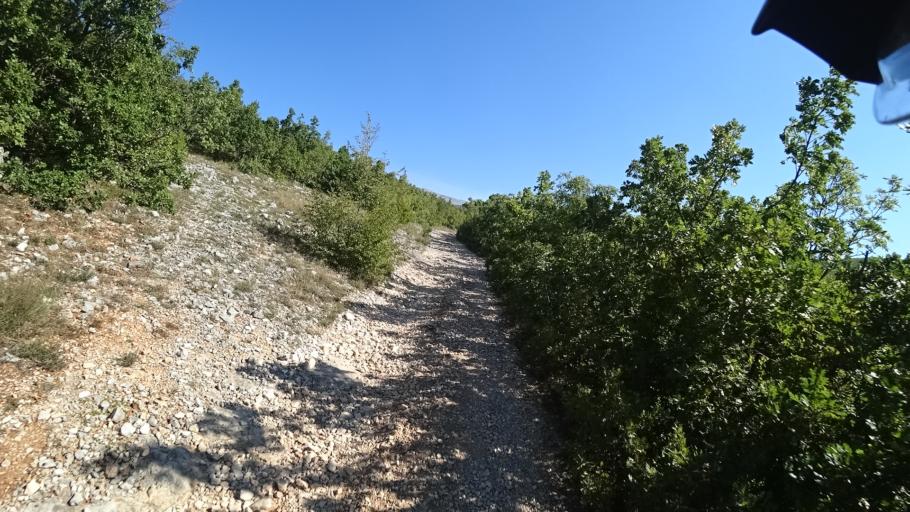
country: HR
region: Splitsko-Dalmatinska
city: Hrvace
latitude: 43.8921
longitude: 16.5190
